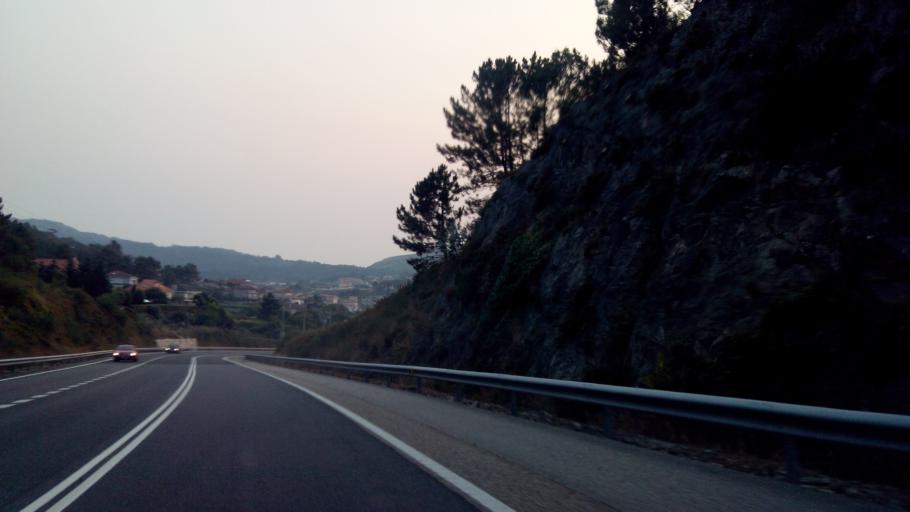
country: ES
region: Galicia
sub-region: Provincia de Pontevedra
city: Baiona
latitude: 42.1143
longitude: -8.8653
